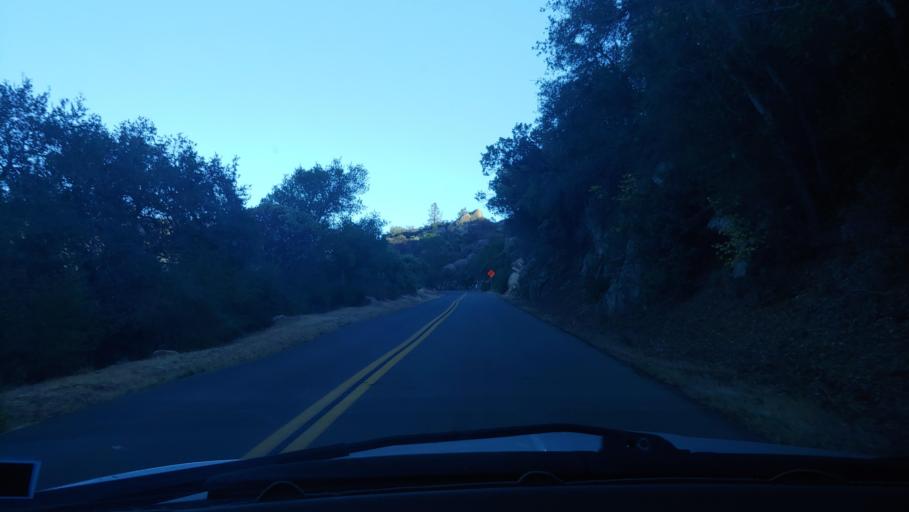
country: US
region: California
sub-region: Santa Barbara County
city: Goleta
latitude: 34.5315
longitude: -119.8369
